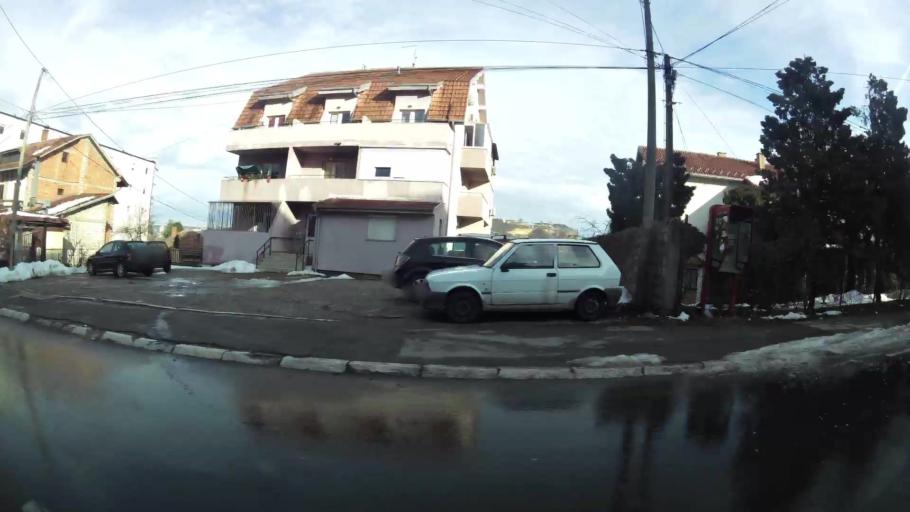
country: RS
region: Central Serbia
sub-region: Belgrade
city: Rakovica
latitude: 44.7315
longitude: 20.4278
